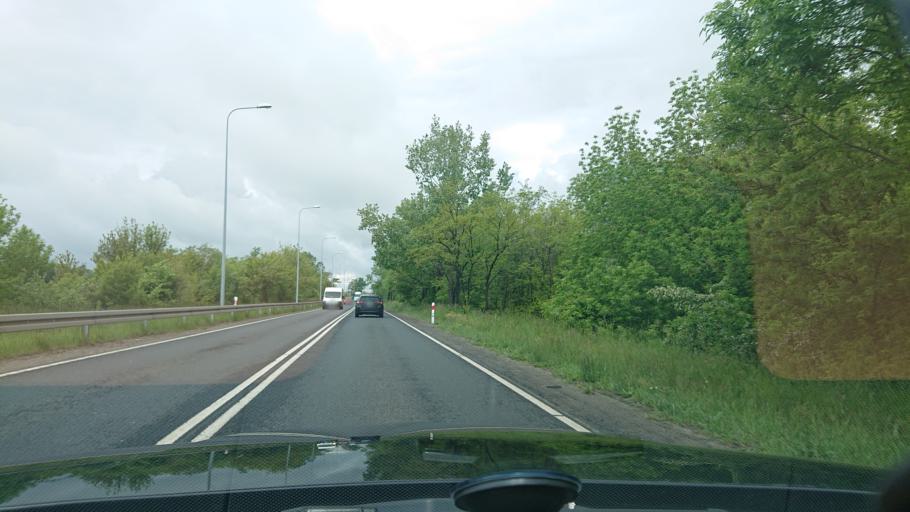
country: PL
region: Greater Poland Voivodeship
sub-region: Powiat gnieznienski
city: Gniezno
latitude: 52.5146
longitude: 17.5906
